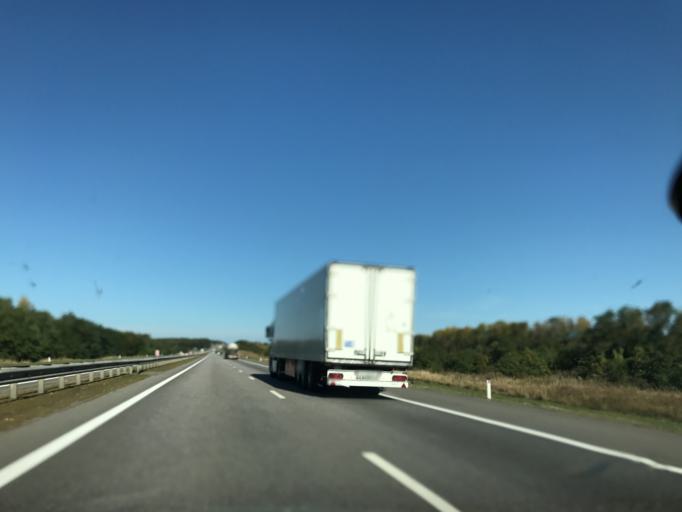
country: RU
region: Voronezj
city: Verkhniy Mamon
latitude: 50.0804
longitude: 40.4417
